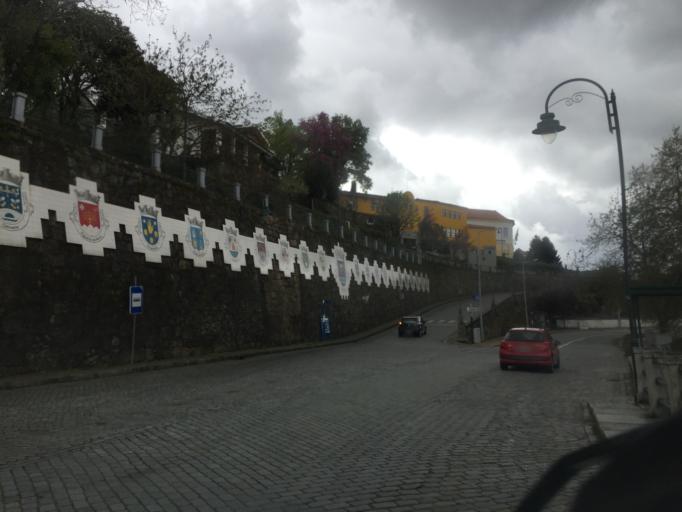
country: PT
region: Guarda
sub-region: Manteigas
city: Manteigas
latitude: 40.4928
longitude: -7.5942
